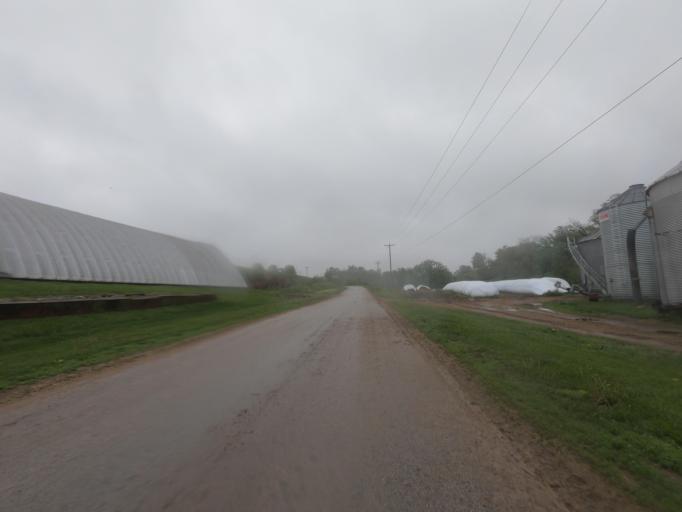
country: US
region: Wisconsin
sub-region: Grant County
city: Hazel Green
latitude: 42.5093
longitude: -90.4689
